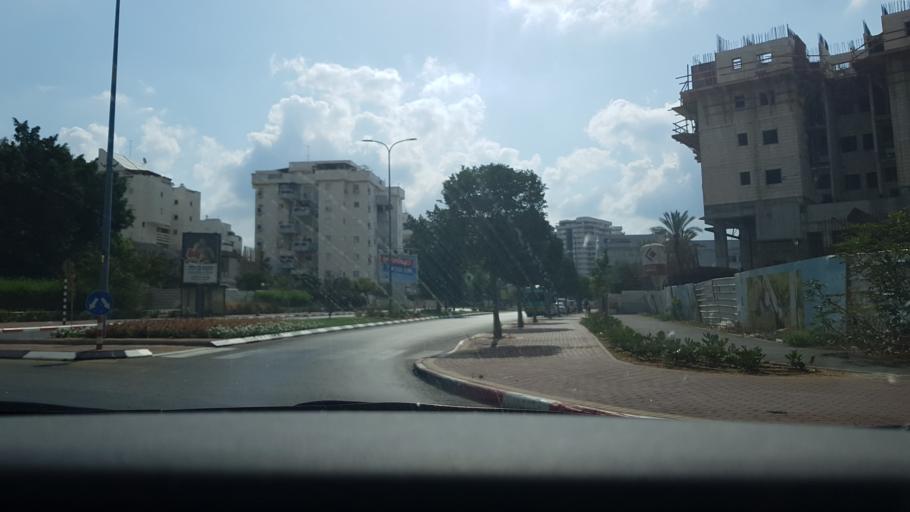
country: IL
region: Central District
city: Mazkeret Batya
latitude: 31.8821
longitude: 34.8115
